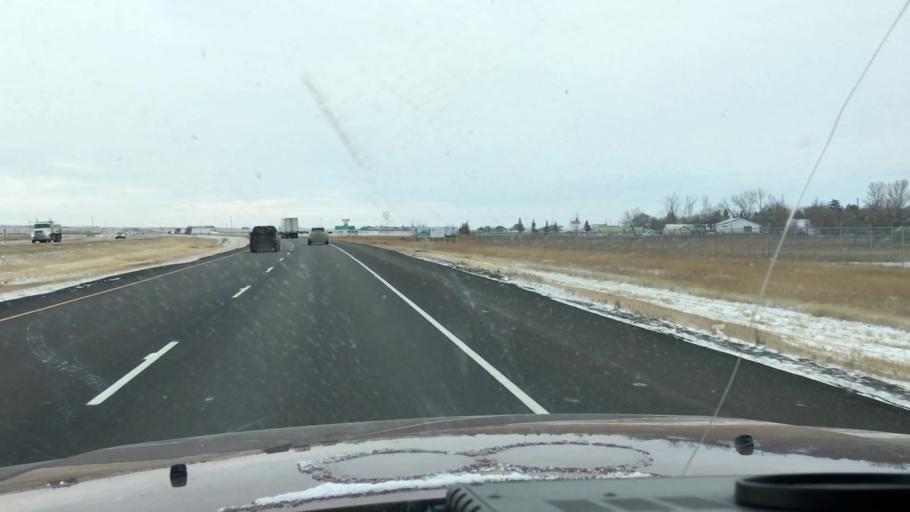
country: CA
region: Saskatchewan
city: Saskatoon
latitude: 51.8145
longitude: -106.4980
